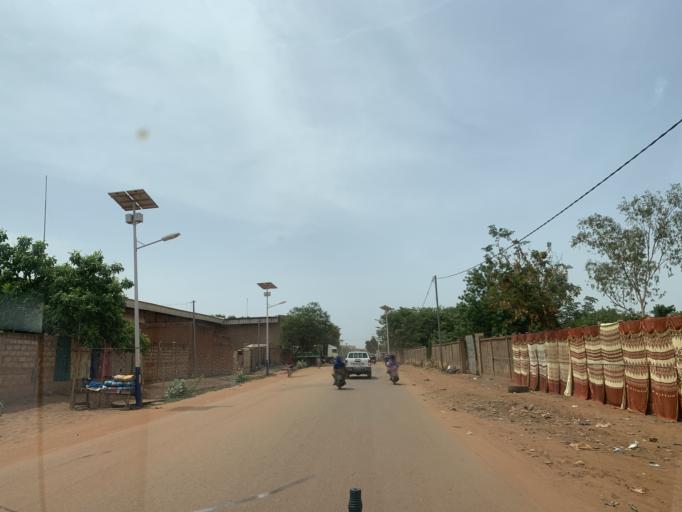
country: BF
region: Centre
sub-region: Kadiogo Province
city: Ouagadougou
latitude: 12.3345
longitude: -1.4965
